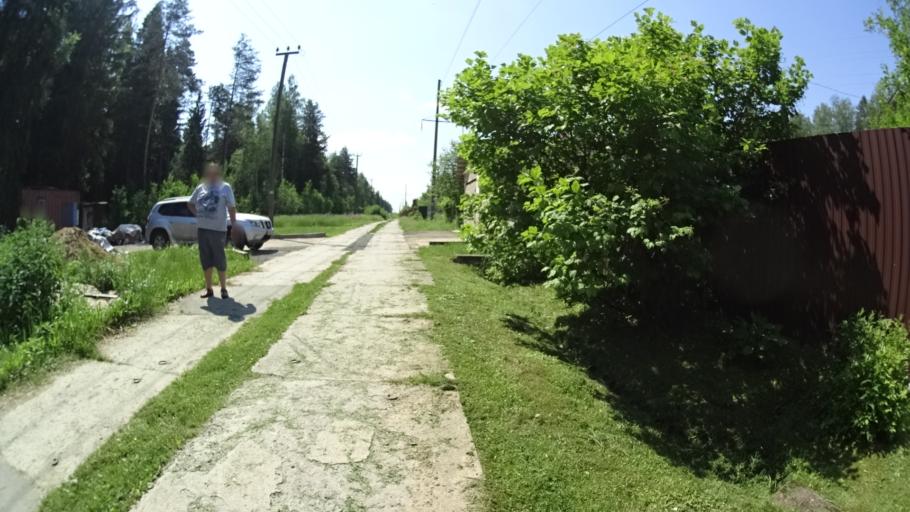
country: RU
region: Moskovskaya
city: Lesnoy
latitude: 56.0832
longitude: 37.9587
